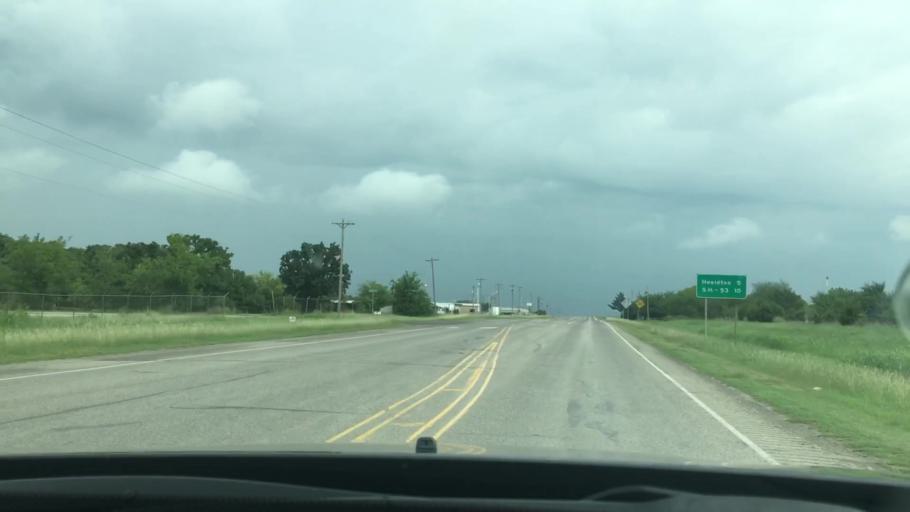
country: US
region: Oklahoma
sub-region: Carter County
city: Wilson
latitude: 34.1744
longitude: -97.4748
